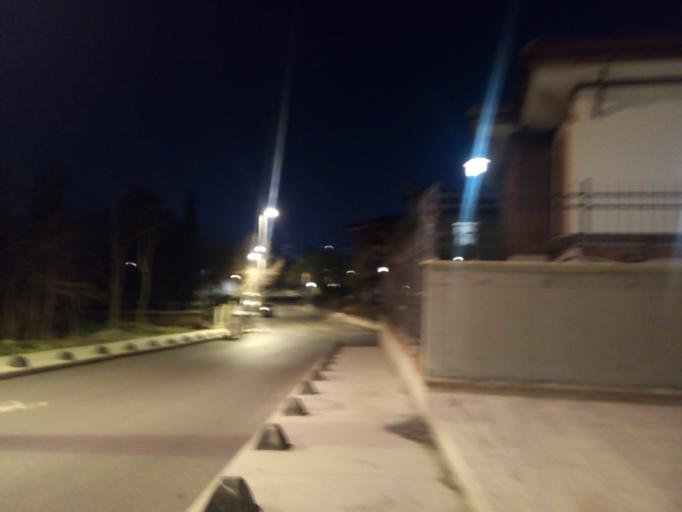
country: TR
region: Istanbul
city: Zeytinburnu
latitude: 41.0139
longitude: 28.9198
